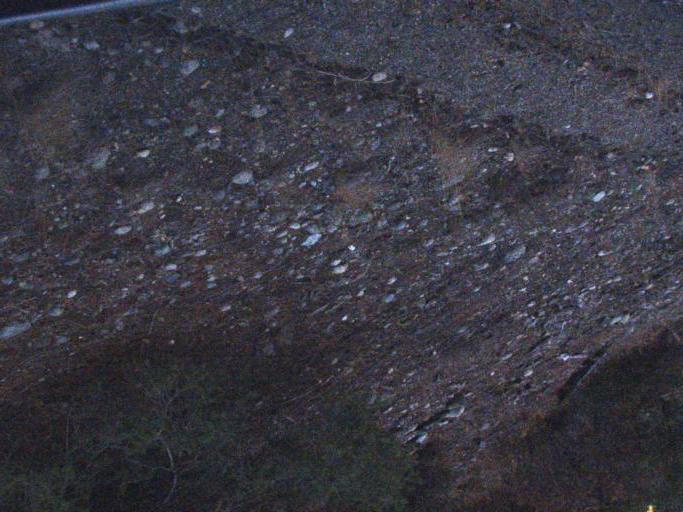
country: US
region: Washington
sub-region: Ferry County
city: Republic
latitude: 48.4213
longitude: -118.7314
